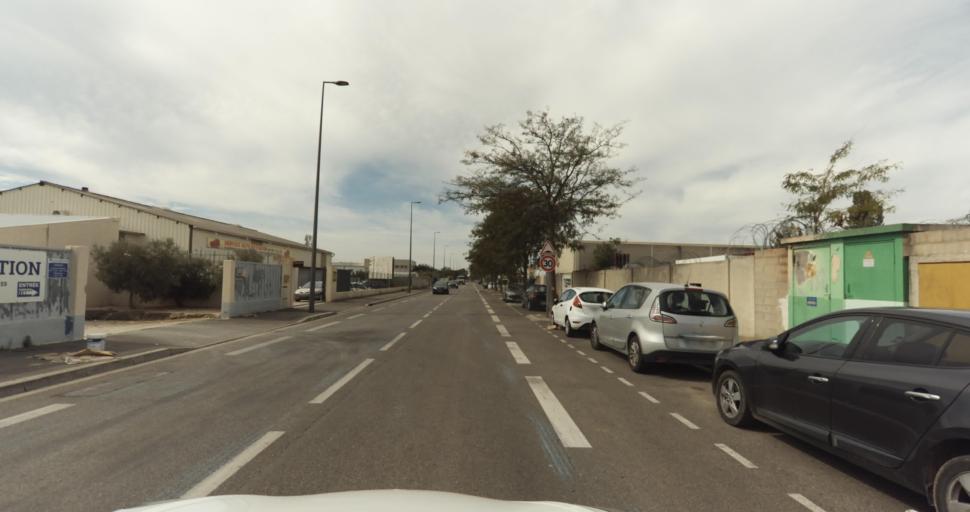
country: FR
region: Provence-Alpes-Cote d'Azur
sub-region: Departement des Bouches-du-Rhone
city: Miramas
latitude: 43.5995
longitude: 4.9999
